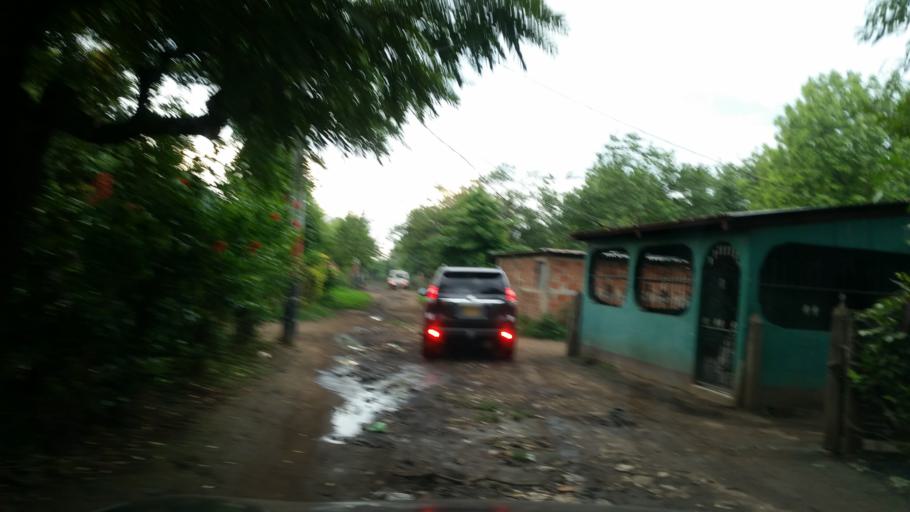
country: NI
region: Chinandega
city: Puerto Morazan
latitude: 12.7655
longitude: -87.1276
